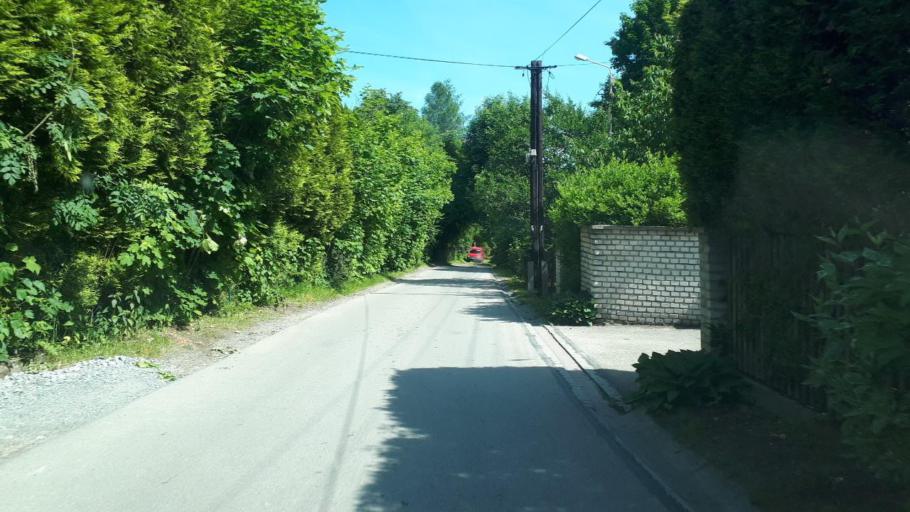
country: PL
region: Silesian Voivodeship
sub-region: Powiat bielski
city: Jaworze
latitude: 49.7882
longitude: 18.9449
